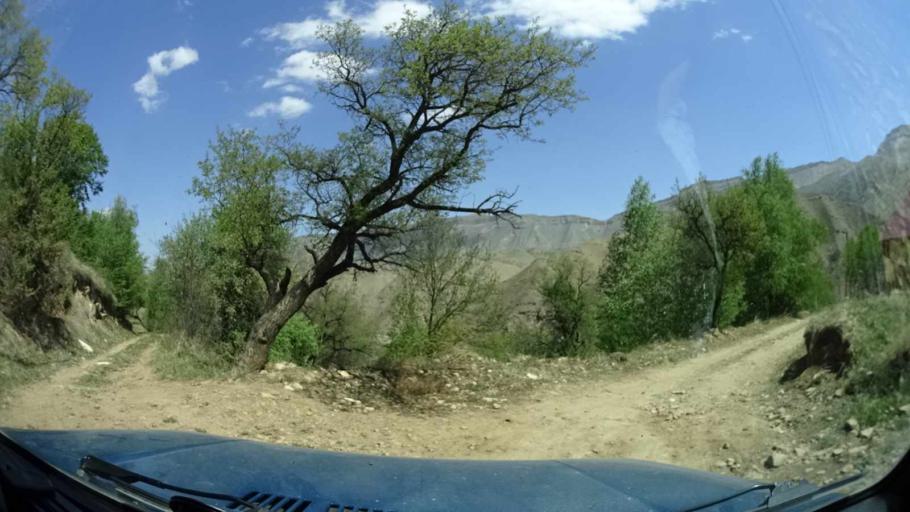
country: RU
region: Dagestan
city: Gunib
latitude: 42.3084
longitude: 47.0040
